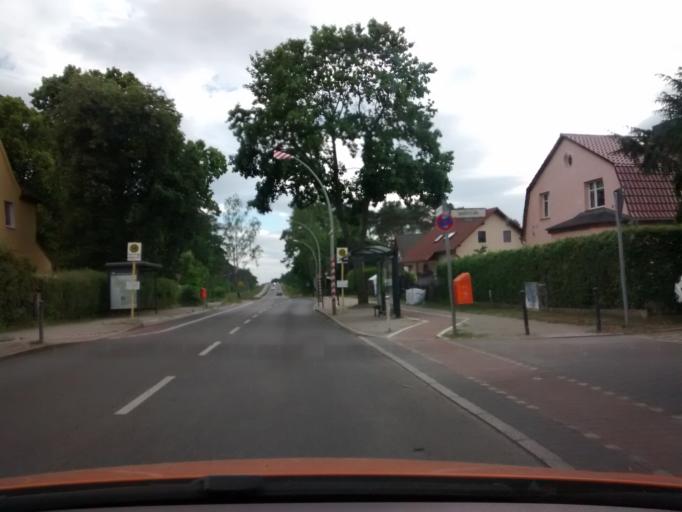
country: DE
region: Berlin
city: Bohnsdorf
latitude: 52.3902
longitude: 13.5711
